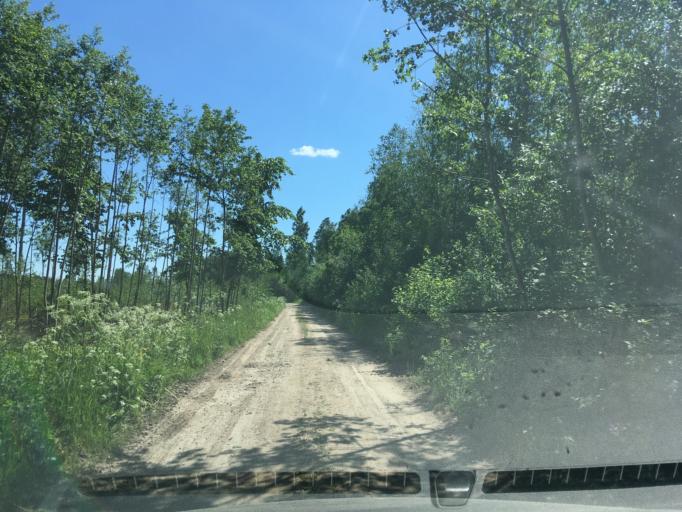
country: EE
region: Harju
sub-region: Raasiku vald
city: Raasiku
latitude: 59.1572
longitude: 25.1363
